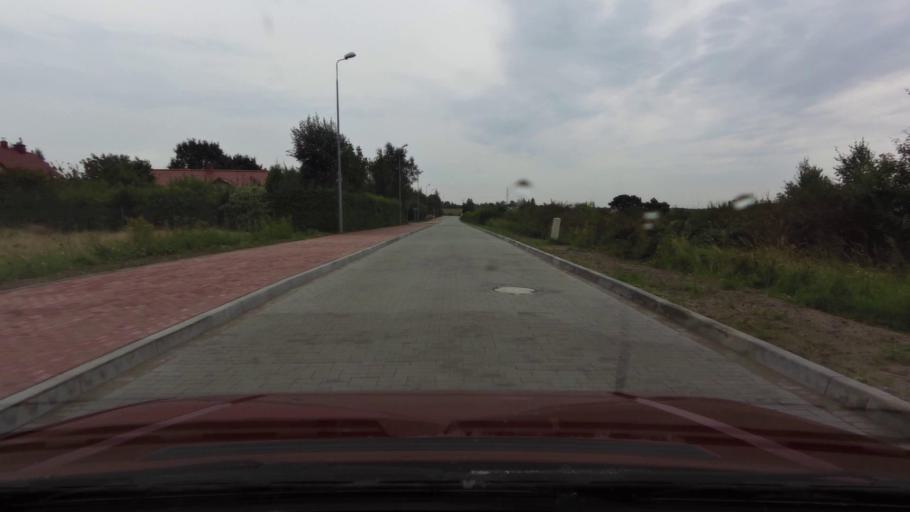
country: PL
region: West Pomeranian Voivodeship
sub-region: Powiat kolobrzeski
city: Grzybowo
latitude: 54.1445
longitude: 15.5252
